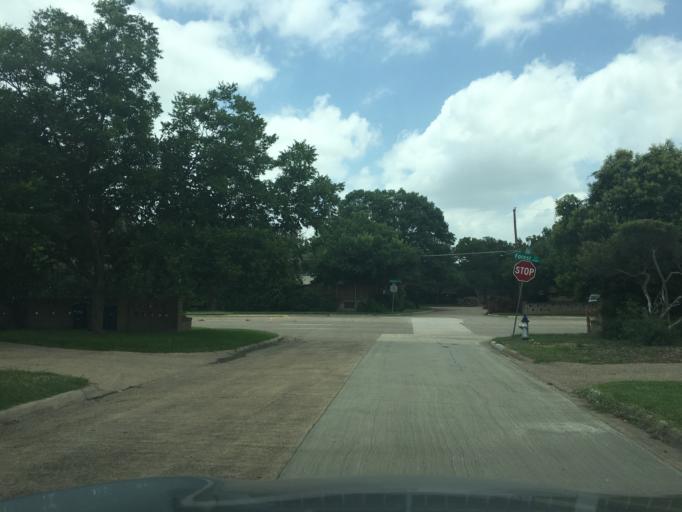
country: US
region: Texas
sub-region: Dallas County
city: Addison
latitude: 32.9091
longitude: -96.8309
